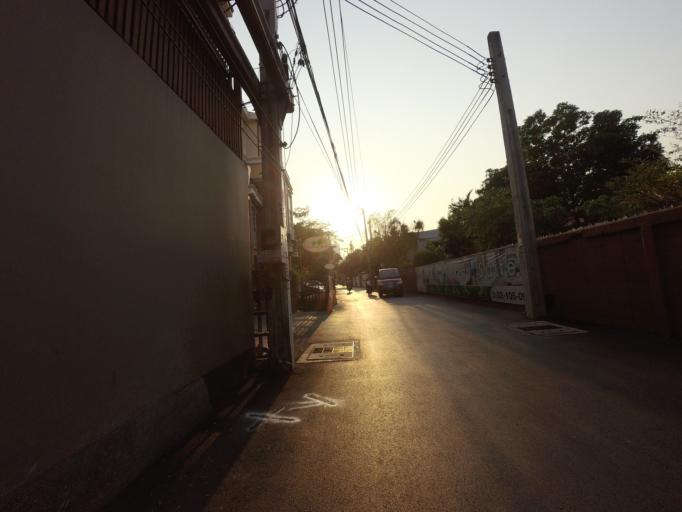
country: TH
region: Bangkok
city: Watthana
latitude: 13.7258
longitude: 100.5906
